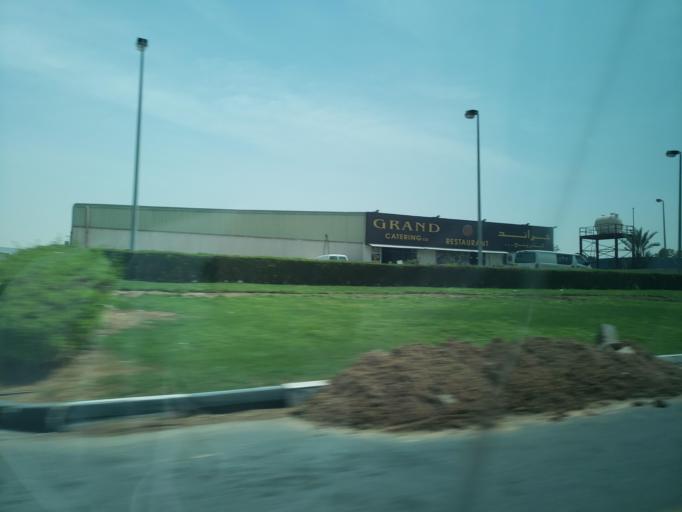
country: AE
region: Ash Shariqah
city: Sharjah
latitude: 25.3314
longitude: 55.4932
